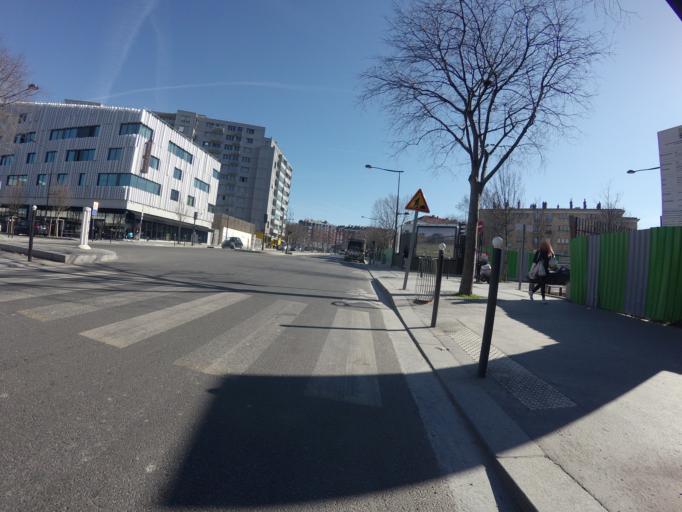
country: FR
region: Ile-de-France
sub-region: Departement des Hauts-de-Seine
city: Clichy
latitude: 48.8991
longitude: 2.3209
